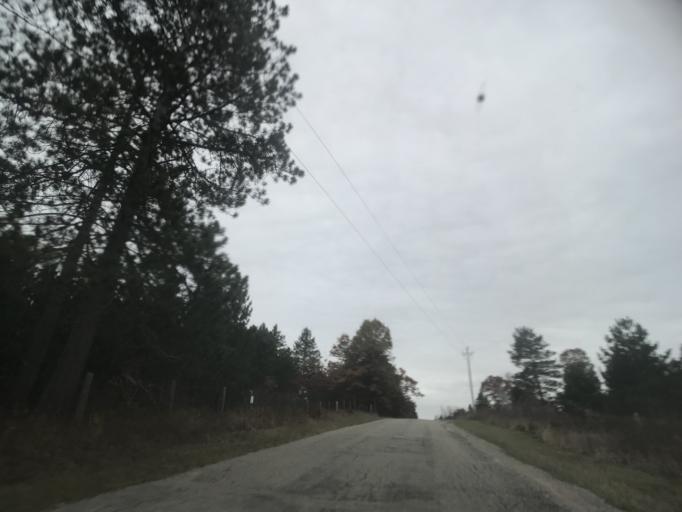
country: US
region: Wisconsin
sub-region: Oconto County
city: Gillett
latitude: 45.3173
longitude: -88.2766
